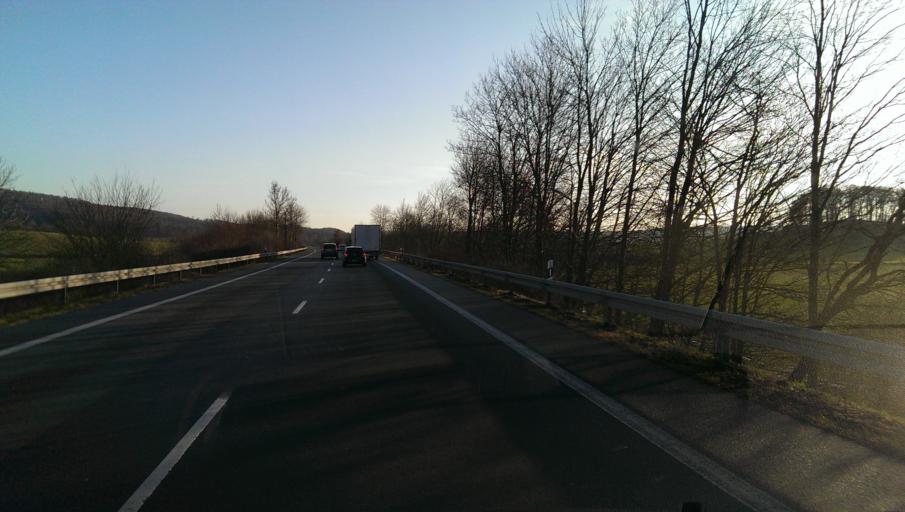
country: DE
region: North Rhine-Westphalia
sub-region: Regierungsbezirk Detmold
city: Bad Driburg
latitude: 51.7113
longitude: 9.0732
